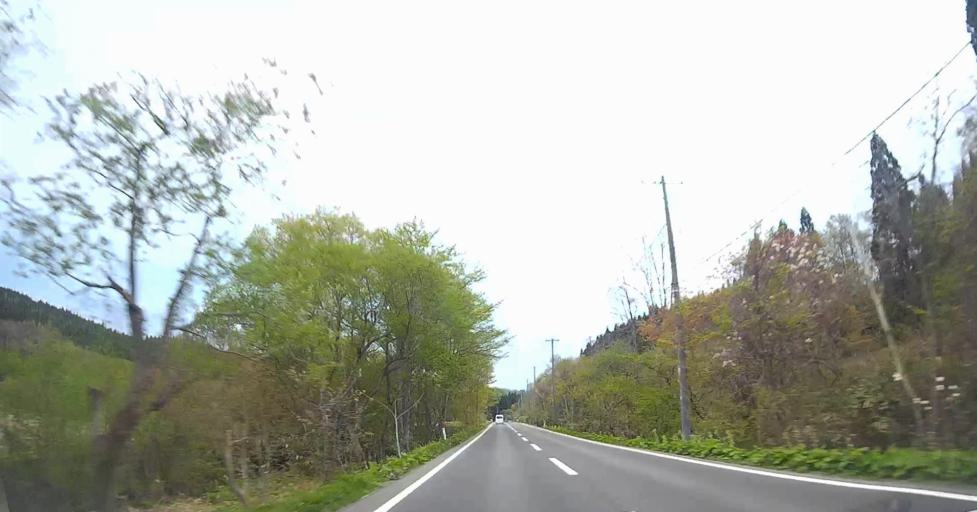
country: JP
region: Aomori
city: Goshogawara
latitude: 41.1235
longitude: 140.5207
